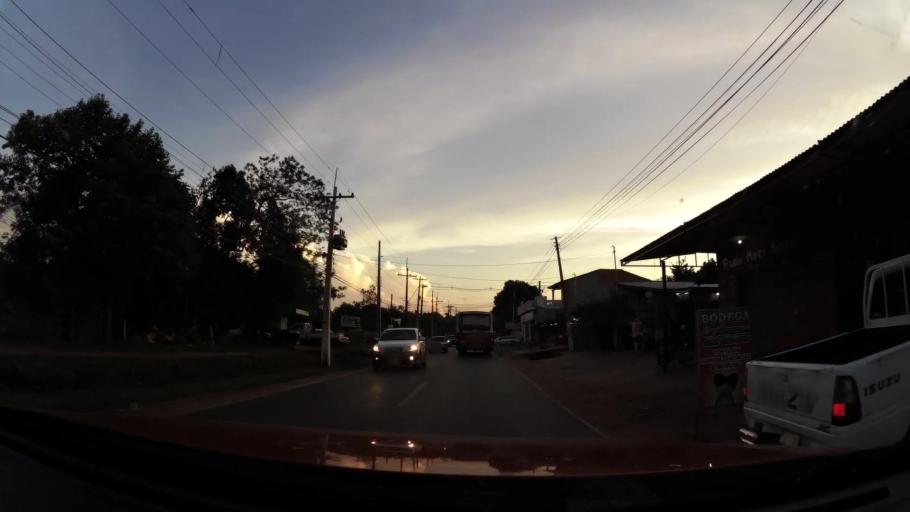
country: PY
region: Central
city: Nemby
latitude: -25.3810
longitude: -57.4941
